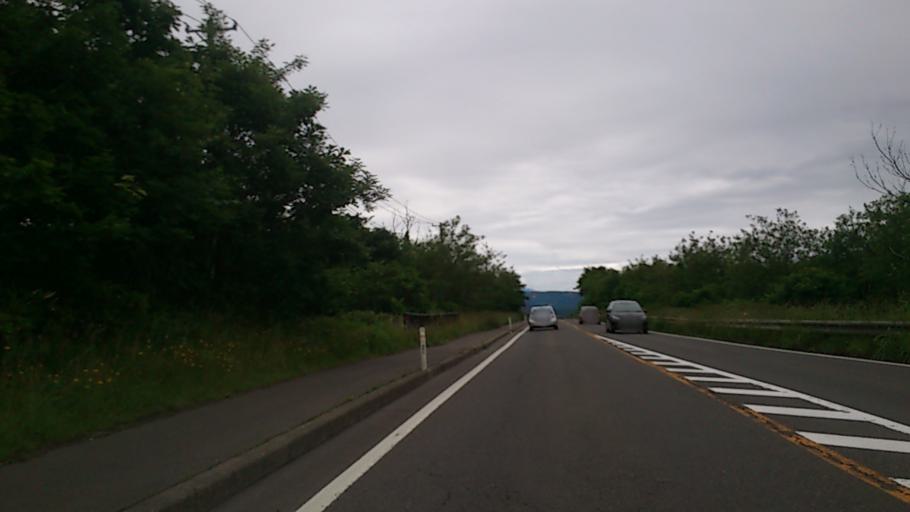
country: JP
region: Akita
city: Akita Shi
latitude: 39.3741
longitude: 140.0176
